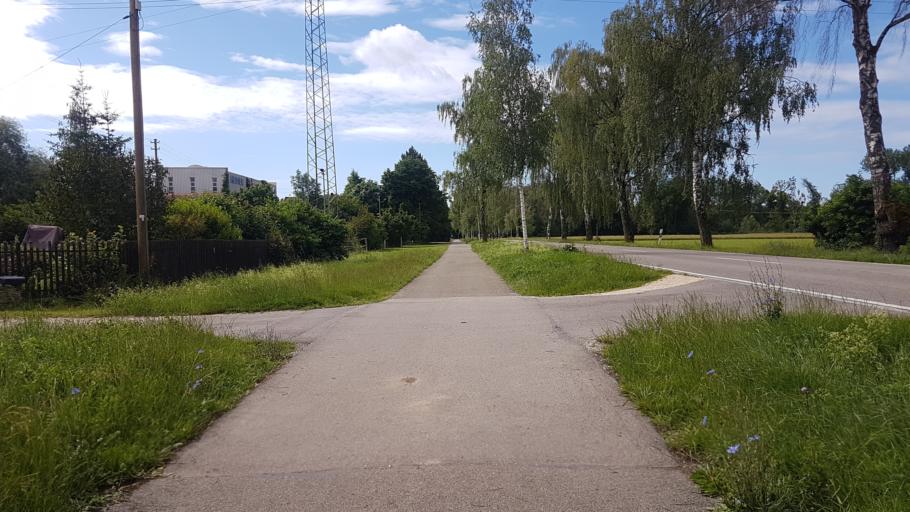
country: DE
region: Bavaria
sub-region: Swabia
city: Guenzburg
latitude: 48.4719
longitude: 10.2637
